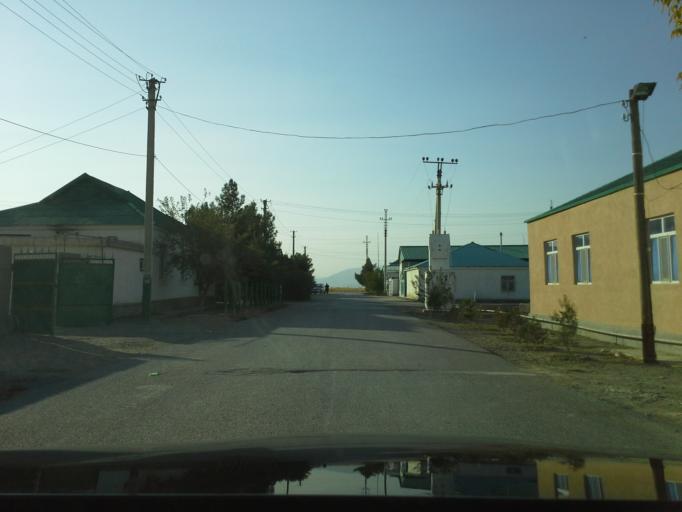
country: TM
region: Ahal
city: Abadan
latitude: 38.0437
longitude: 58.1649
